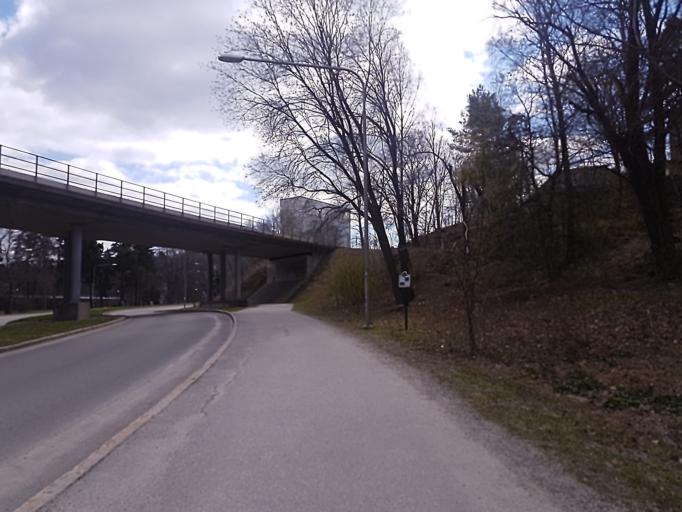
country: SE
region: Stockholm
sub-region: Nacka Kommun
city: Nacka
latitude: 59.2930
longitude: 18.1142
